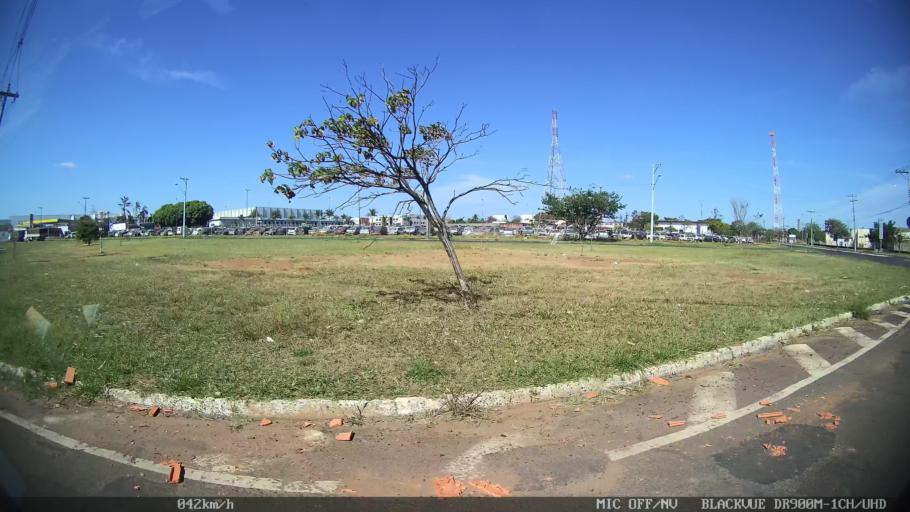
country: BR
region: Sao Paulo
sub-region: Franca
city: Franca
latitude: -20.5497
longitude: -47.4430
